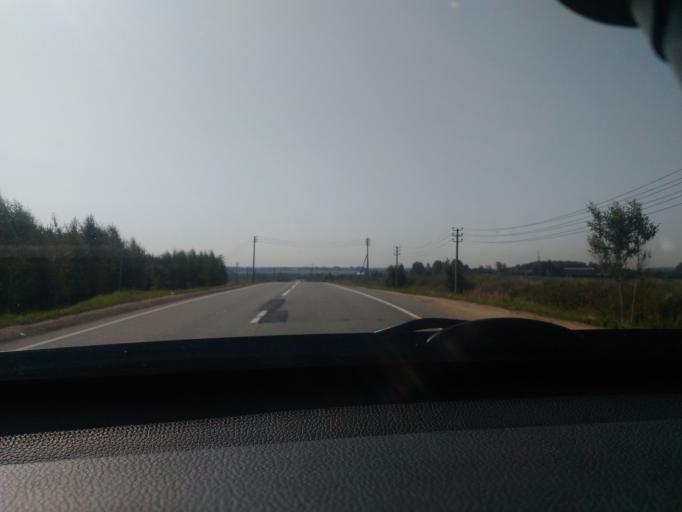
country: RU
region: Moskovskaya
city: Dedenevo
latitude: 56.2405
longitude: 37.5481
